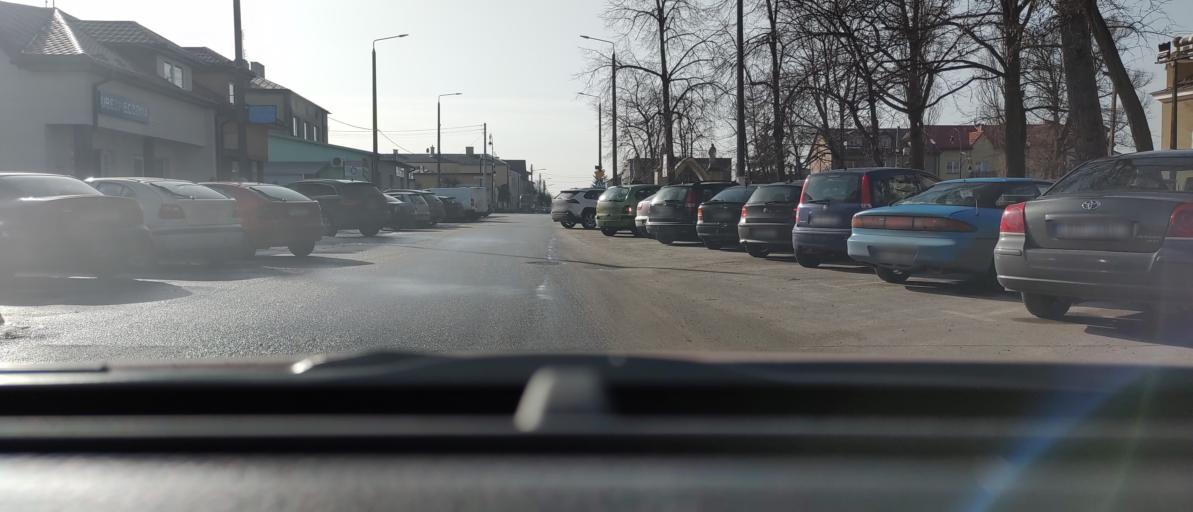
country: PL
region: Masovian Voivodeship
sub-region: Powiat bialobrzeski
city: Bialobrzegi
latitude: 51.6507
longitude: 20.9550
